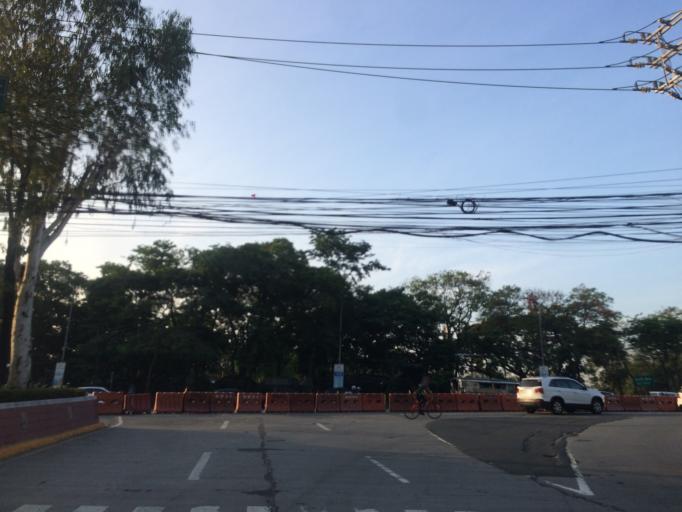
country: PH
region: Metro Manila
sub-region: Quezon City
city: Quezon City
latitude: 14.6545
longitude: 121.0473
